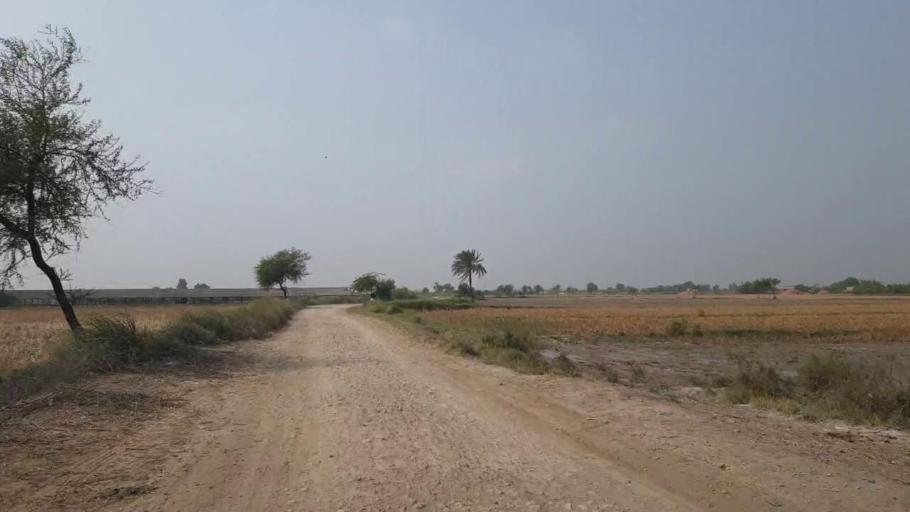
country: PK
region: Sindh
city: Kario
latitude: 24.8777
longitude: 68.5075
